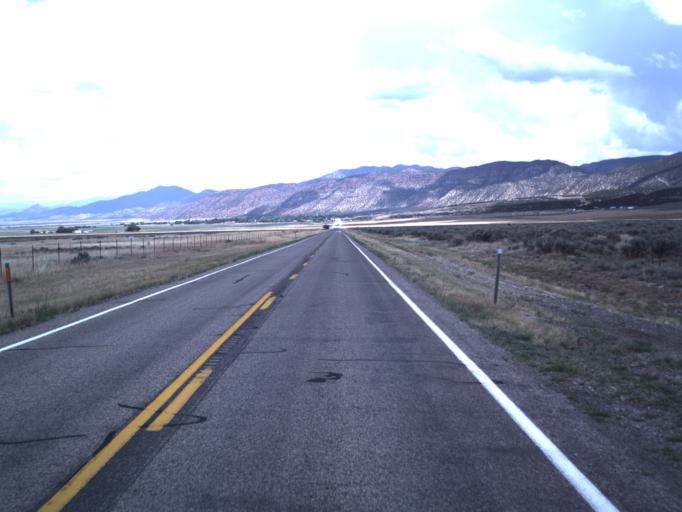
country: US
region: Utah
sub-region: Iron County
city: Parowan
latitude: 37.8567
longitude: -112.8179
